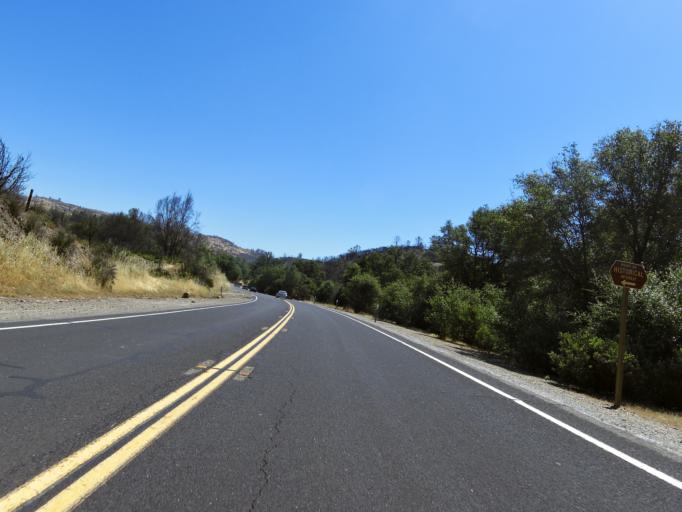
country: US
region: California
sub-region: Mariposa County
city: Mariposa
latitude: 37.4800
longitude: -120.0129
